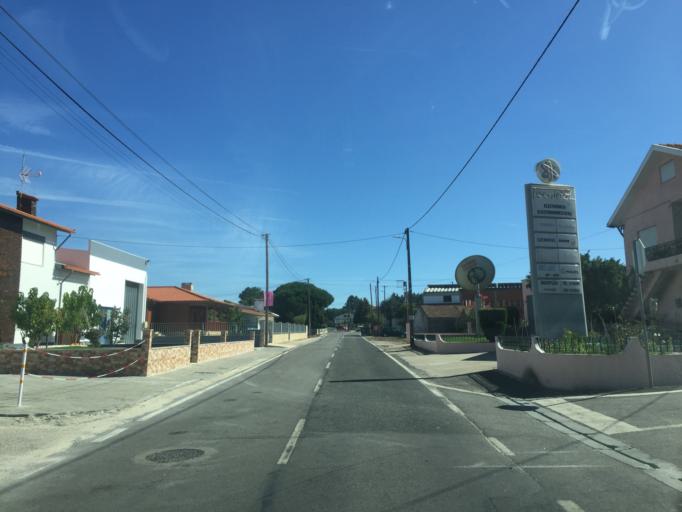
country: PT
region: Coimbra
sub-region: Figueira da Foz
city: Alhadas
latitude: 40.2182
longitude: -8.8133
